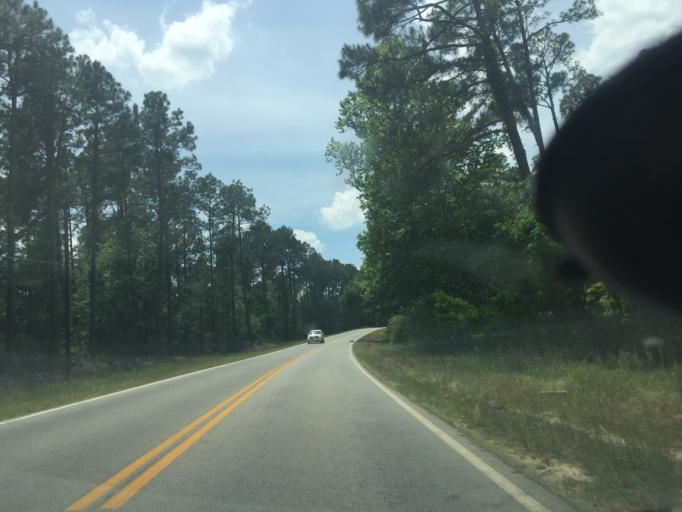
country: US
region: Georgia
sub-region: Bulloch County
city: Statesboro
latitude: 32.4156
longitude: -81.8236
